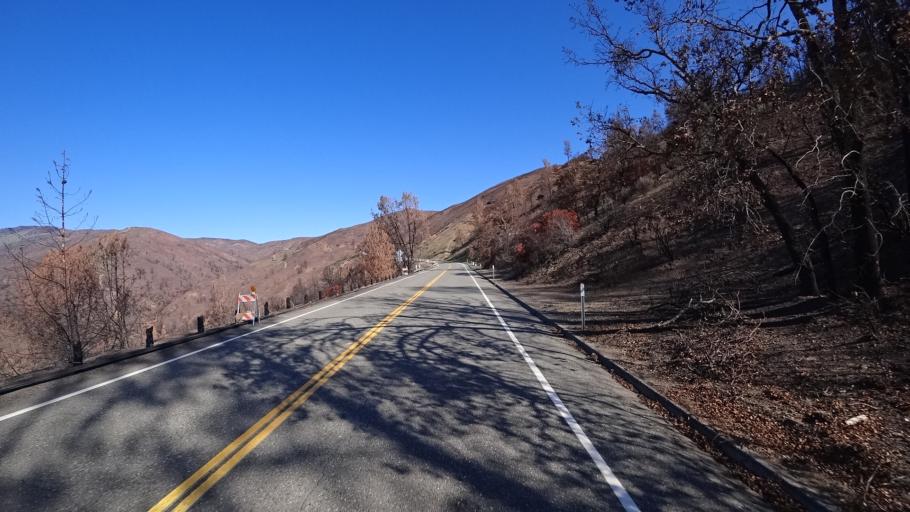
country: US
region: California
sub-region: Glenn County
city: Orland
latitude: 39.6405
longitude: -122.6052
